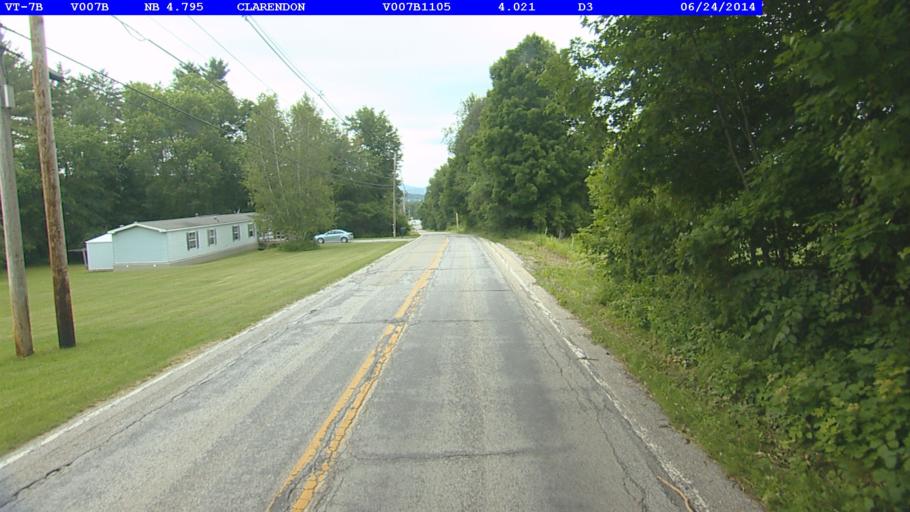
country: US
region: Vermont
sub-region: Rutland County
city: Rutland
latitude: 43.5561
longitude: -72.9601
